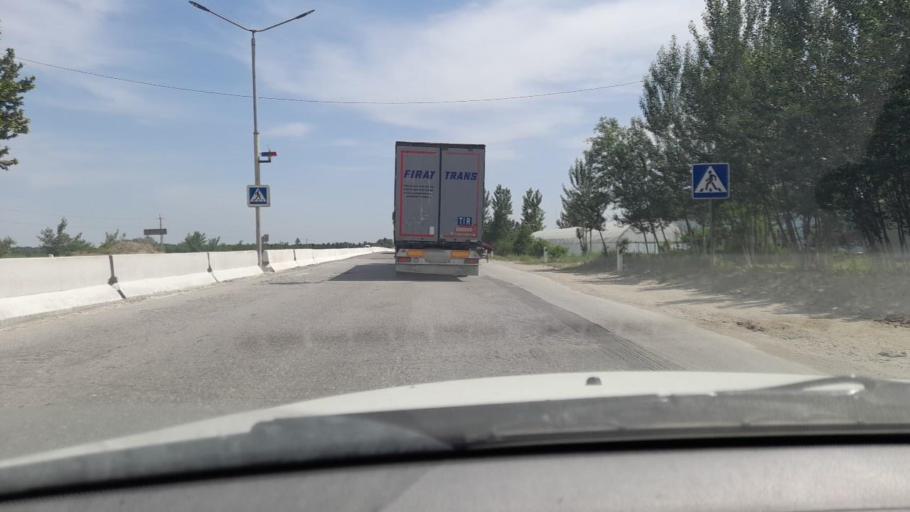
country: UZ
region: Navoiy
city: Navoiy
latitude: 40.0789
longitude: 65.6100
